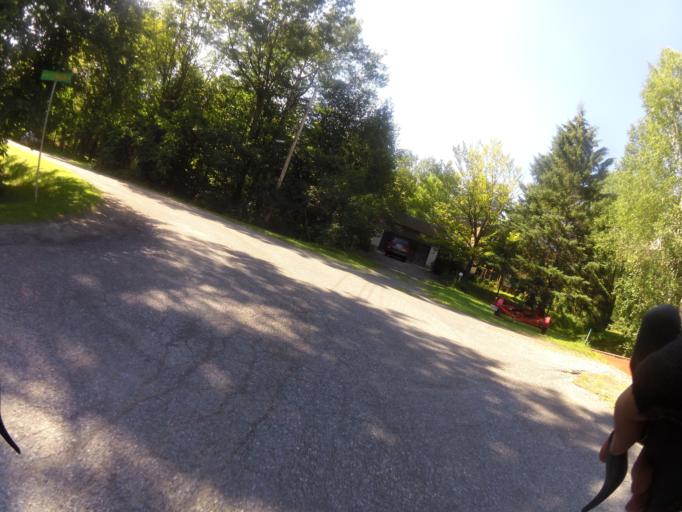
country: CA
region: Ontario
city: Ottawa
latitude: 45.3222
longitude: -75.6904
